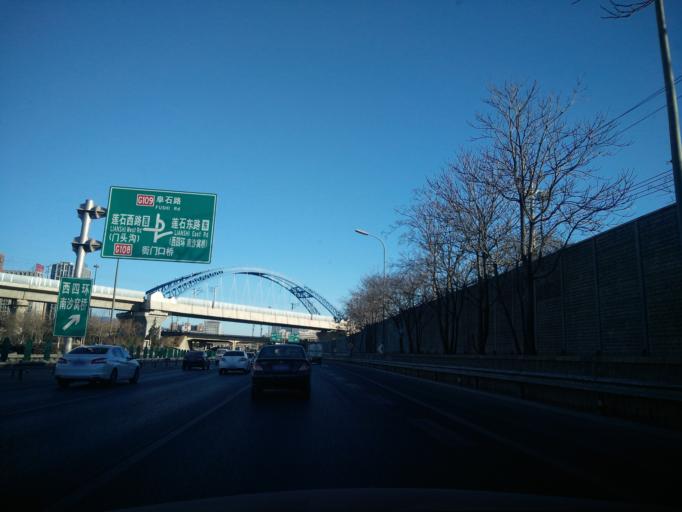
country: CN
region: Beijing
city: Lugu
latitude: 39.8890
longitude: 116.2054
